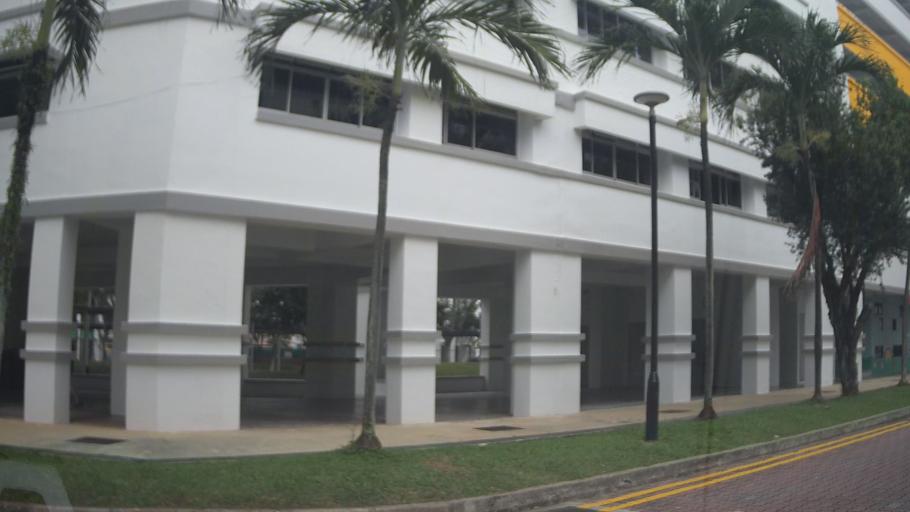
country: MY
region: Johor
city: Johor Bahru
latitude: 1.3991
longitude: 103.7448
